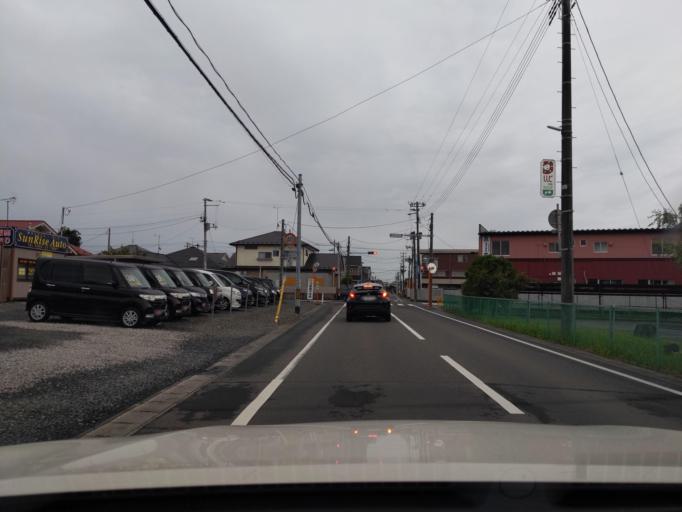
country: JP
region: Miyagi
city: Ishinomaki
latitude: 38.4344
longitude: 141.2648
